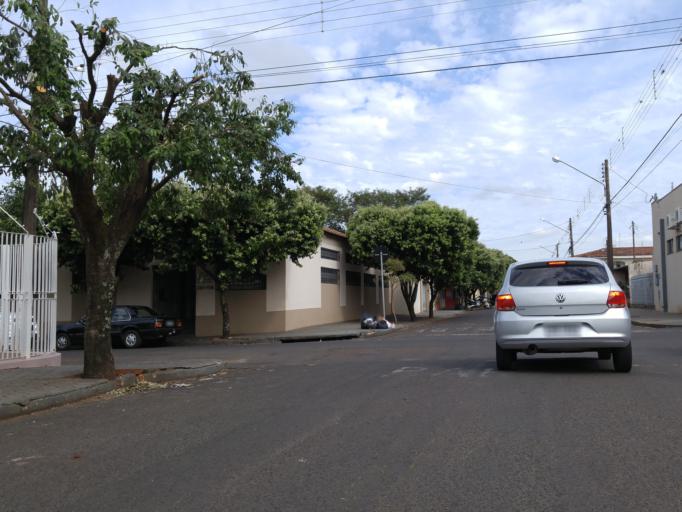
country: BR
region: Sao Paulo
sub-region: Paraguacu Paulista
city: Paraguacu Paulista
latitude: -22.4162
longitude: -50.5767
